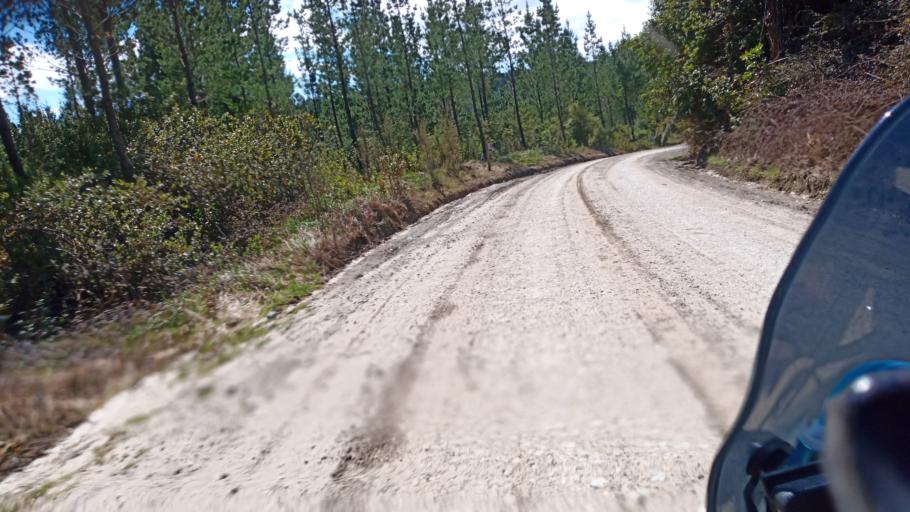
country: NZ
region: Gisborne
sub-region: Gisborne District
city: Gisborne
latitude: -38.9084
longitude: 177.8088
